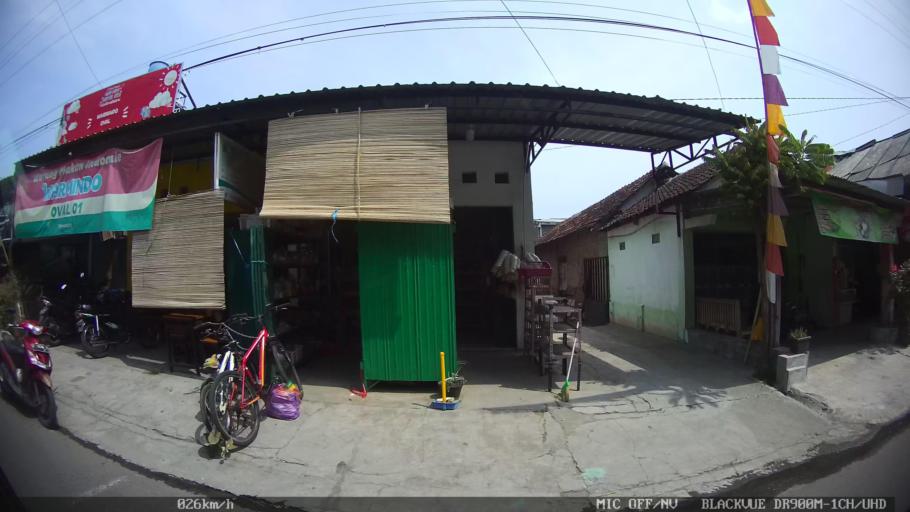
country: ID
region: Daerah Istimewa Yogyakarta
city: Depok
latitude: -7.7935
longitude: 110.4042
